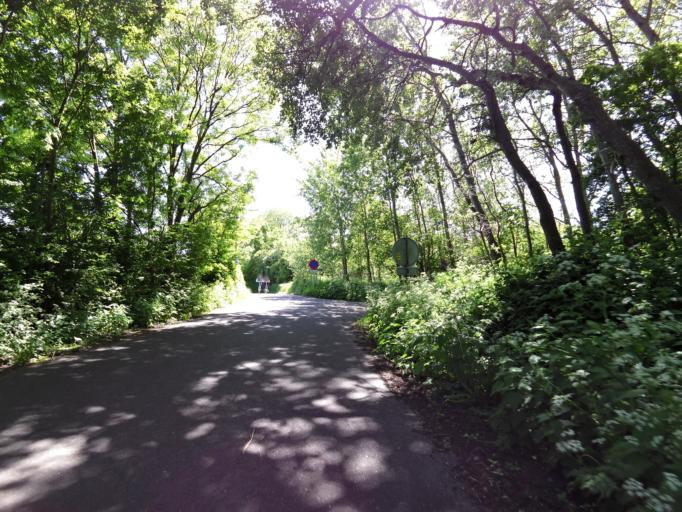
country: NL
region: South Holland
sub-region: Gemeente Hellevoetsluis
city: Nieuw-Helvoet
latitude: 51.8428
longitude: 4.0835
